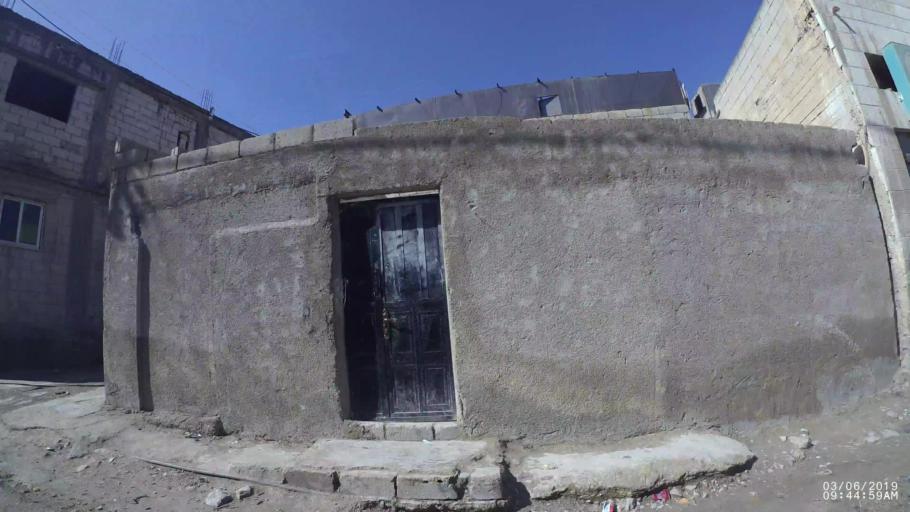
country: JO
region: Amman
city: Amman
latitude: 31.9887
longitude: 35.9856
